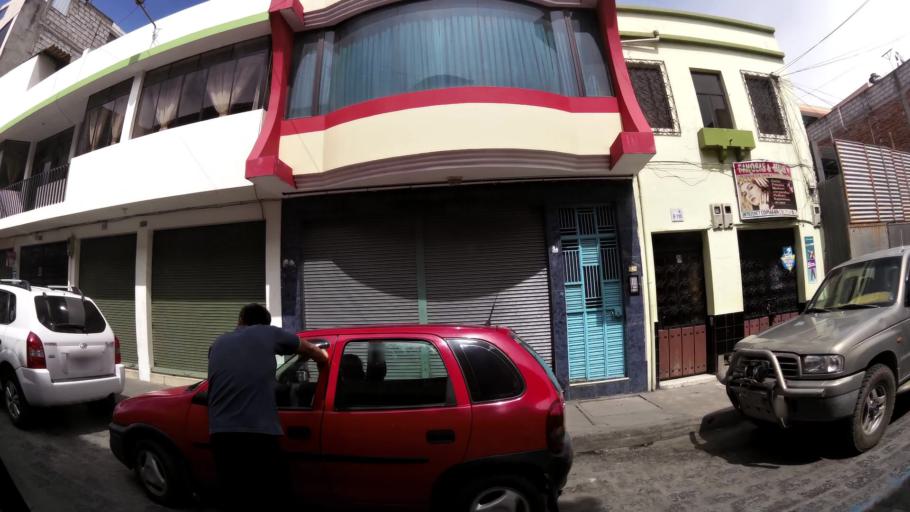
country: EC
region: Cotopaxi
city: Latacunga
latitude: -0.9307
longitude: -78.6170
